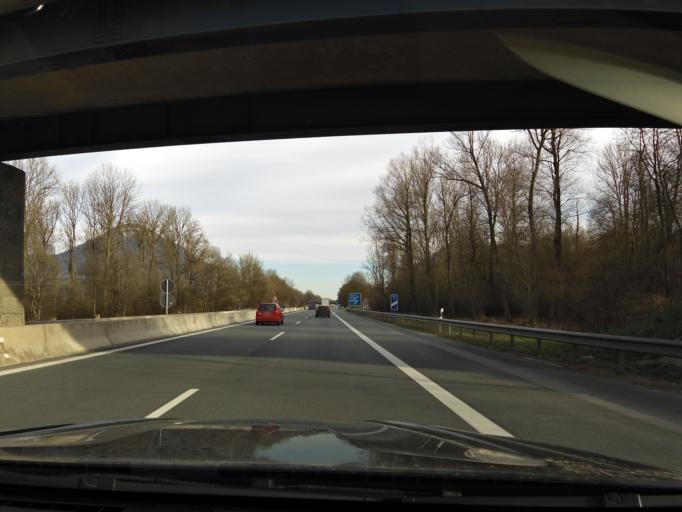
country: DE
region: Bavaria
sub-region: Upper Bavaria
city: Oberaudorf
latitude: 47.6416
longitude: 12.1924
